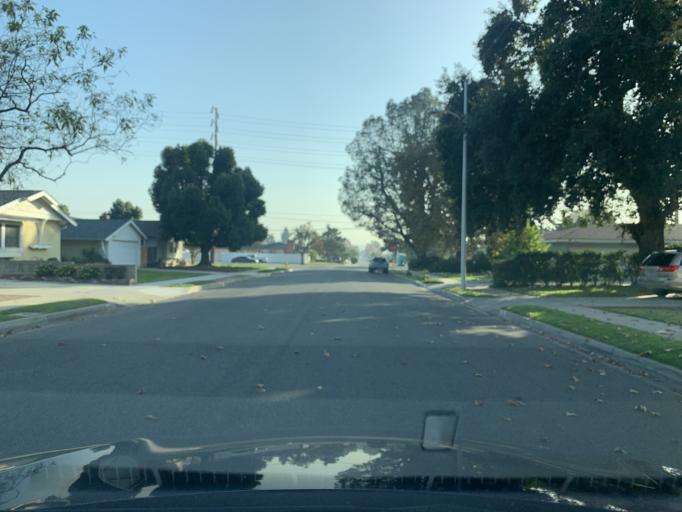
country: US
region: California
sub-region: Los Angeles County
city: Covina
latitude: 34.0902
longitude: -117.9011
